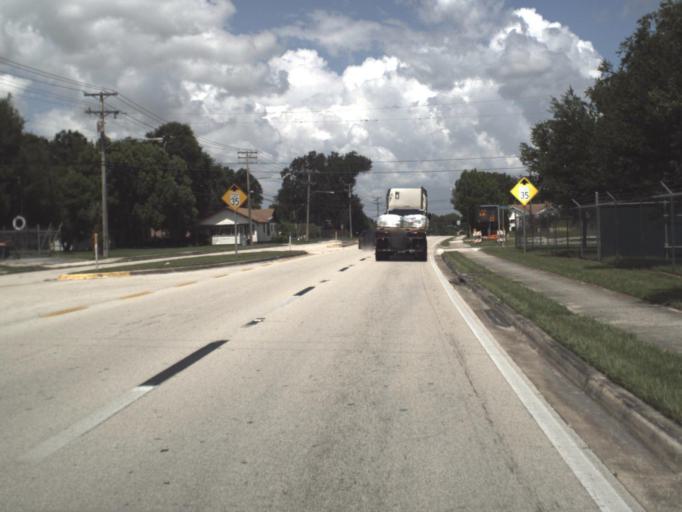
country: US
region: Florida
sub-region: Polk County
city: Bartow
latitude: 27.8881
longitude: -81.8281
